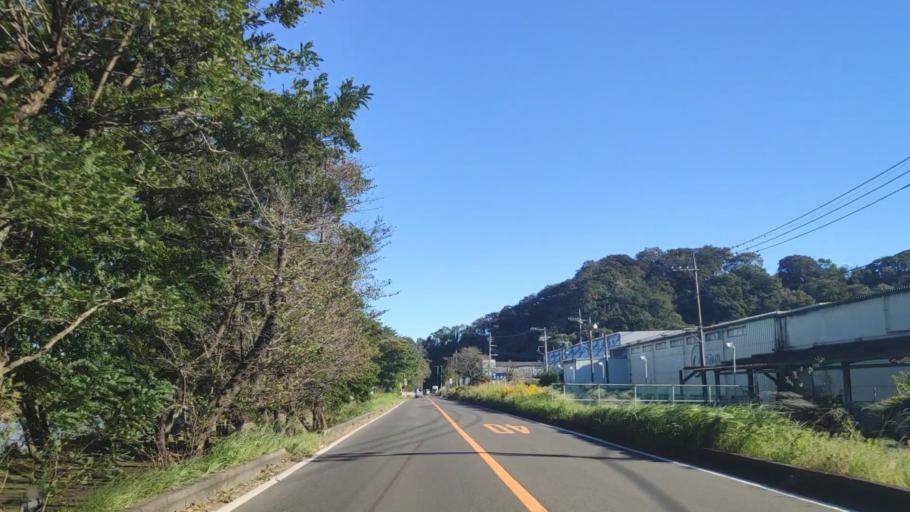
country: JP
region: Kanagawa
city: Zama
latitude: 35.5331
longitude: 139.3403
